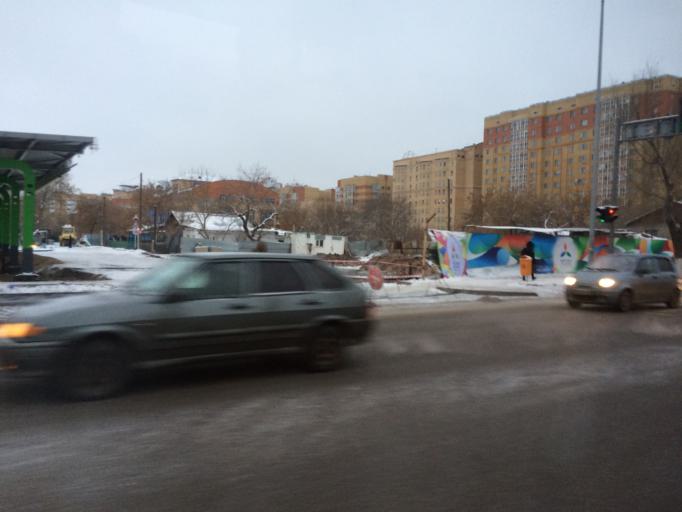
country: KZ
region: Astana Qalasy
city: Astana
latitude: 51.1612
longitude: 71.4417
